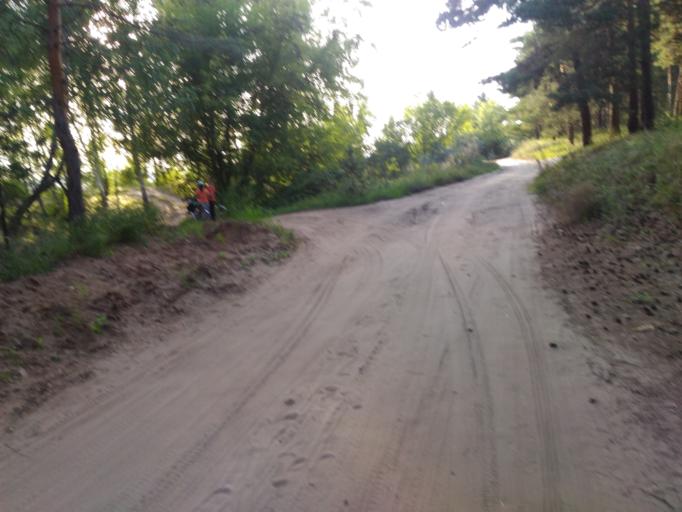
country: RU
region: Ulyanovsk
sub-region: Ulyanovskiy Rayon
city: Ulyanovsk
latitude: 54.3573
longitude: 48.5154
